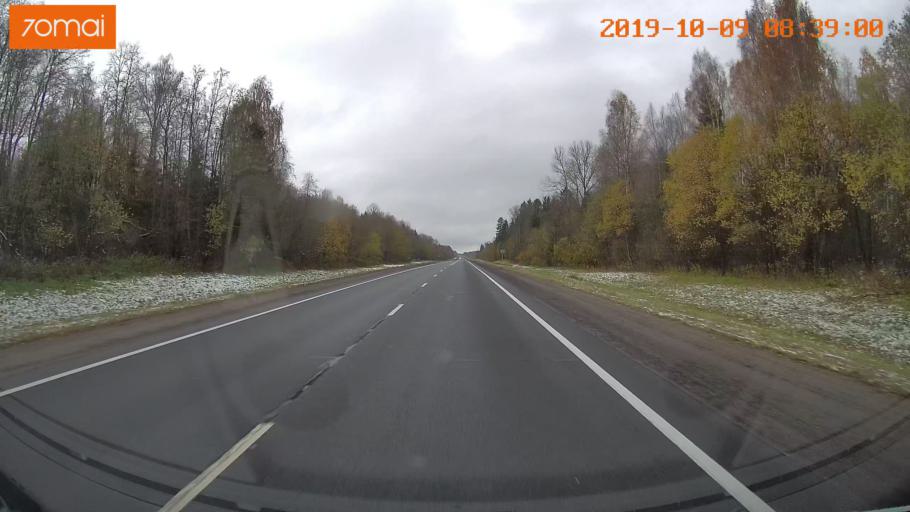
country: RU
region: Vologda
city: Gryazovets
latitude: 58.9649
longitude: 40.1587
